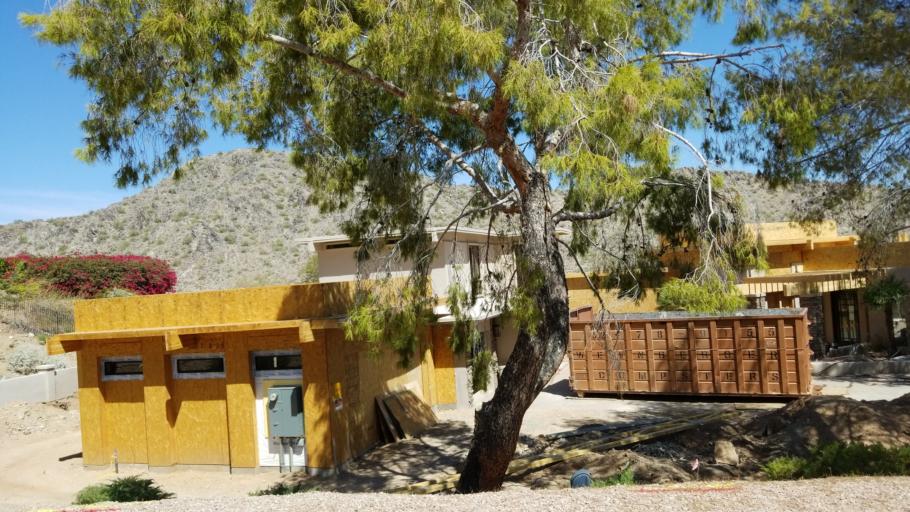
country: US
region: Arizona
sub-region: Maricopa County
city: Paradise Valley
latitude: 33.5619
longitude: -111.9855
